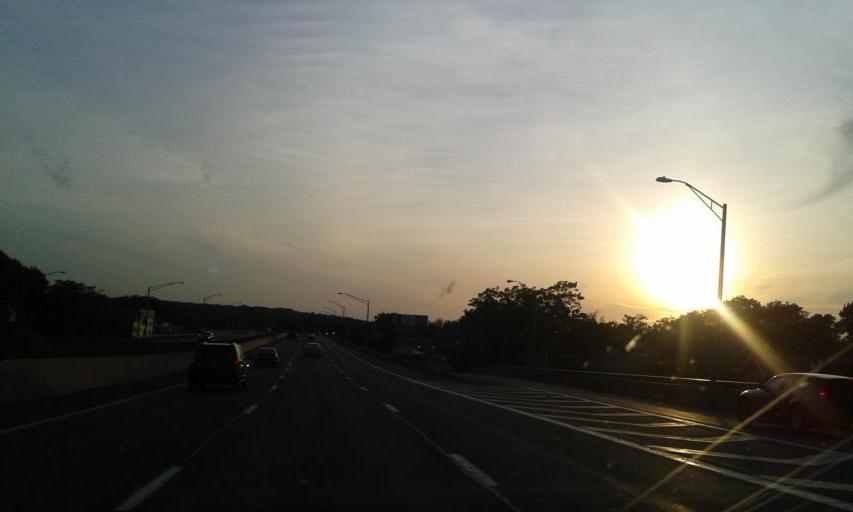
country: US
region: New York
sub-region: Onondaga County
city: Syracuse
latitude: 43.0559
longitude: -76.1674
